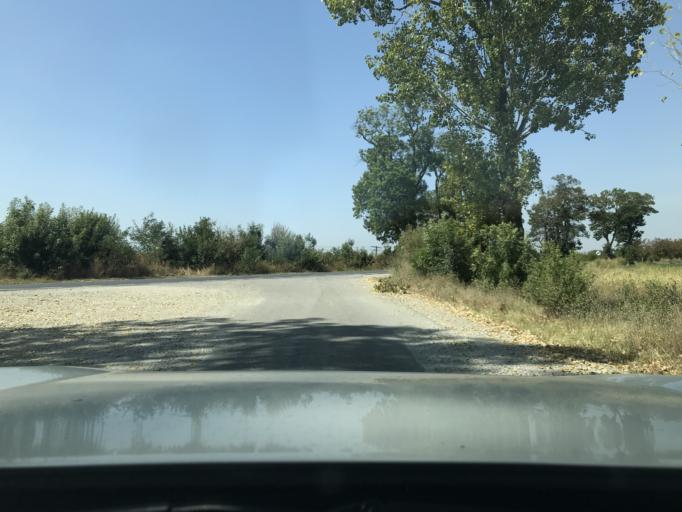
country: RO
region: Olt
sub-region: Comuna Osica de Sus
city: Osica de Sus
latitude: 44.2356
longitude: 24.3375
